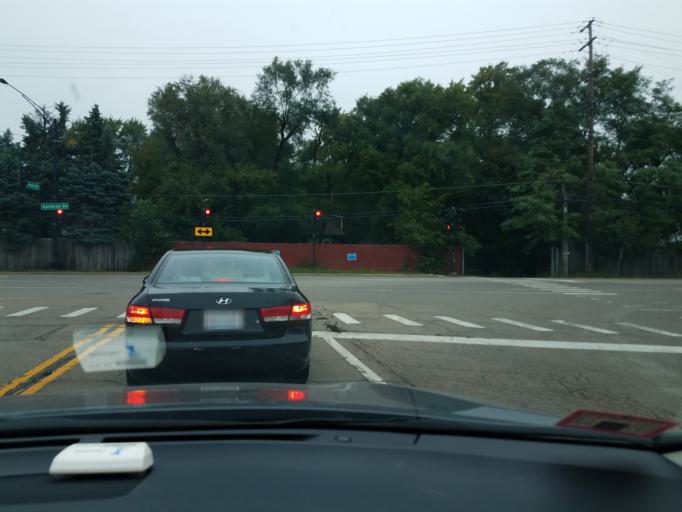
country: US
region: Illinois
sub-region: Cook County
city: Buffalo Grove
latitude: 42.1825
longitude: -87.9489
